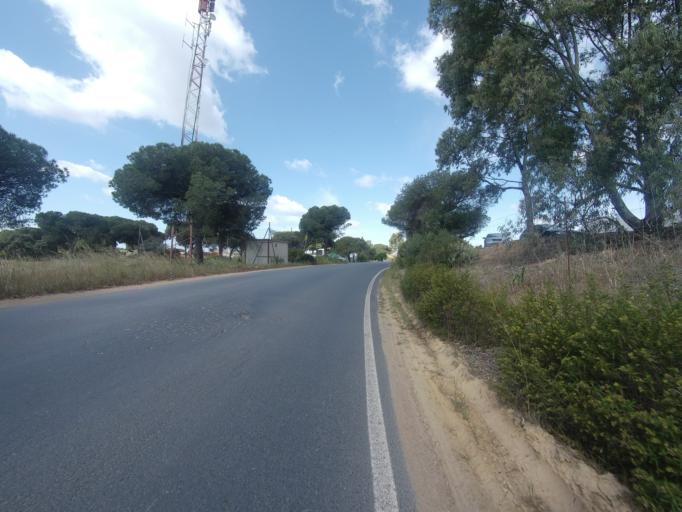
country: ES
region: Andalusia
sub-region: Provincia de Huelva
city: Aljaraque
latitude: 37.2451
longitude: -7.0299
